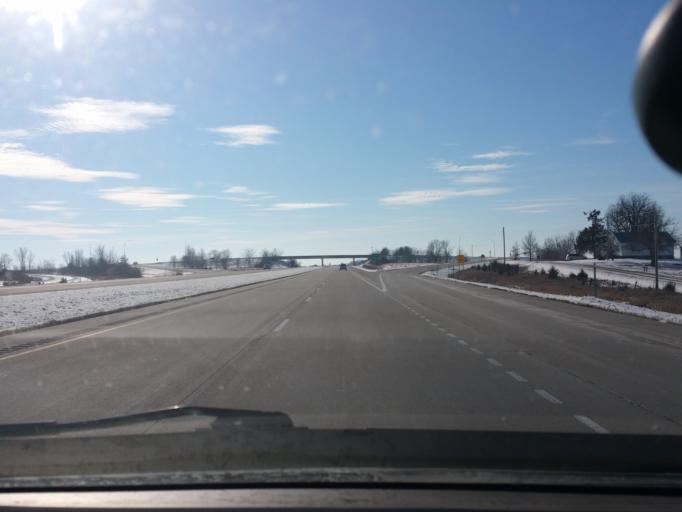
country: US
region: Iowa
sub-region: Clarke County
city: Osceola
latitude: 40.9764
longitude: -93.7978
